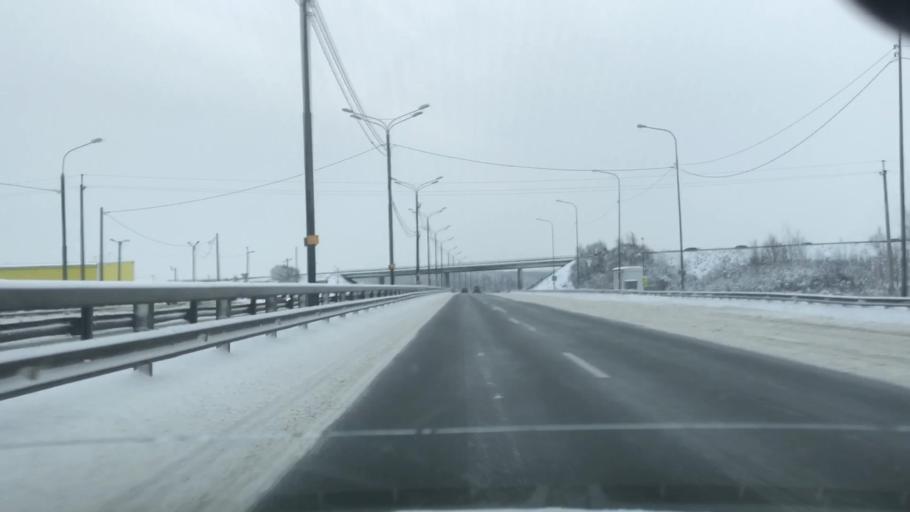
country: RU
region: Moskovskaya
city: Barybino
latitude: 55.2852
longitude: 37.8575
